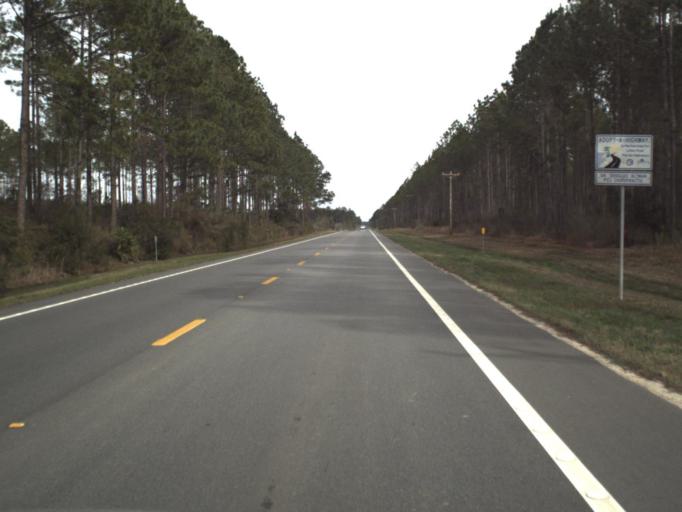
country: US
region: Florida
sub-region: Gulf County
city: Wewahitchka
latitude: 30.1439
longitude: -85.2964
